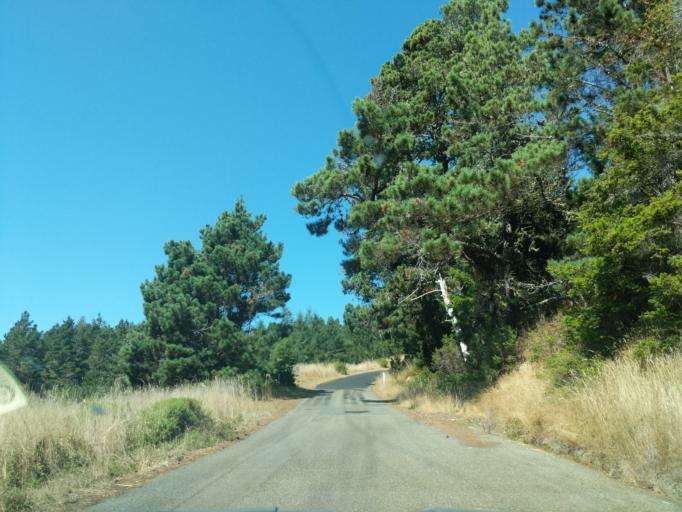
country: US
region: California
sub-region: Sonoma County
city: Monte Rio
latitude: 38.5200
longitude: -123.2442
